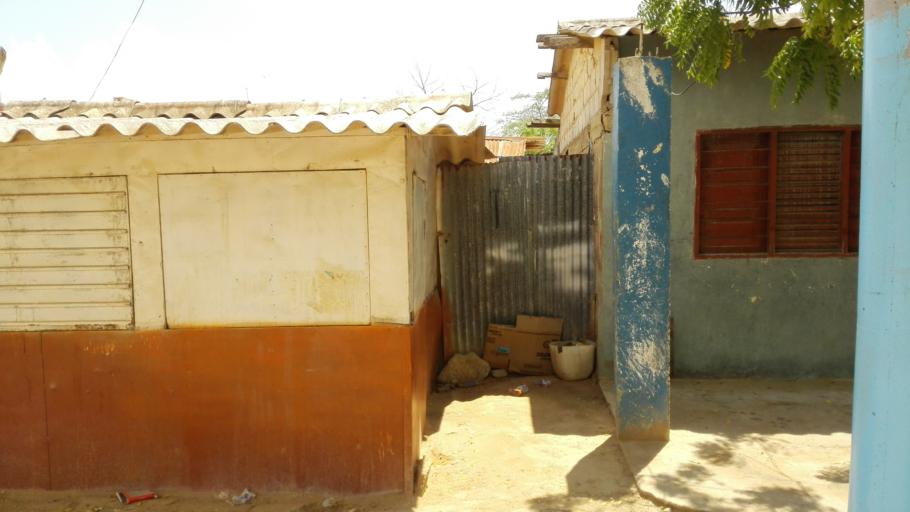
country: CO
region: La Guajira
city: Manaure
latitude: 11.7709
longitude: -72.4455
